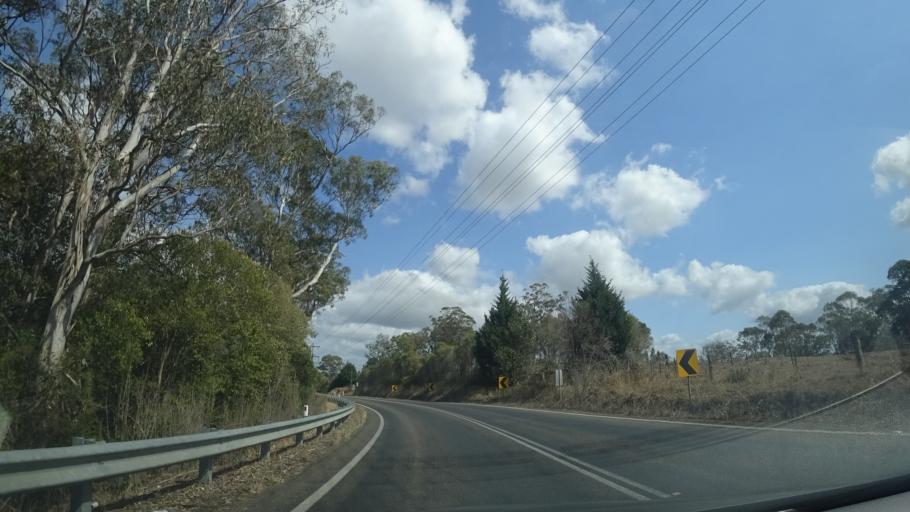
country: AU
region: New South Wales
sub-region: Wollondilly
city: Picton
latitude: -34.1869
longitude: 150.5929
